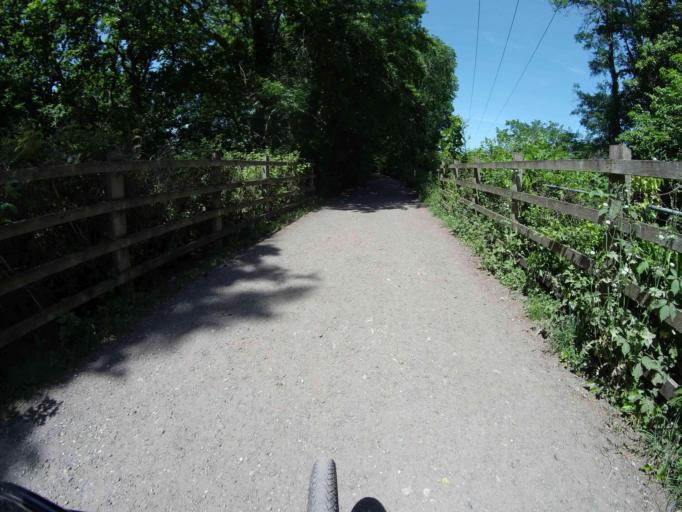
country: GB
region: England
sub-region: Devon
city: Bovey Tracey
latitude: 50.5956
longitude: -3.6826
